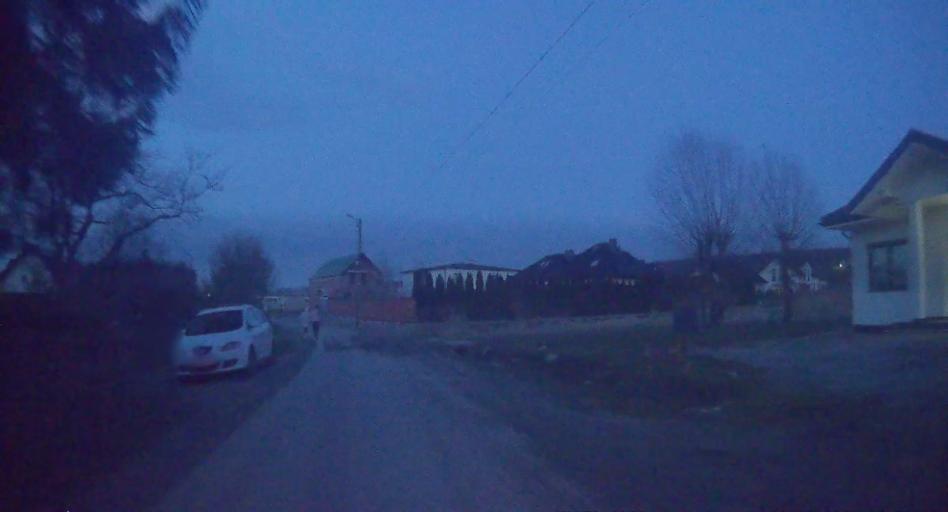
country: PL
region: Subcarpathian Voivodeship
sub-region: Powiat debicki
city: Debica
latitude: 50.0265
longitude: 21.3891
